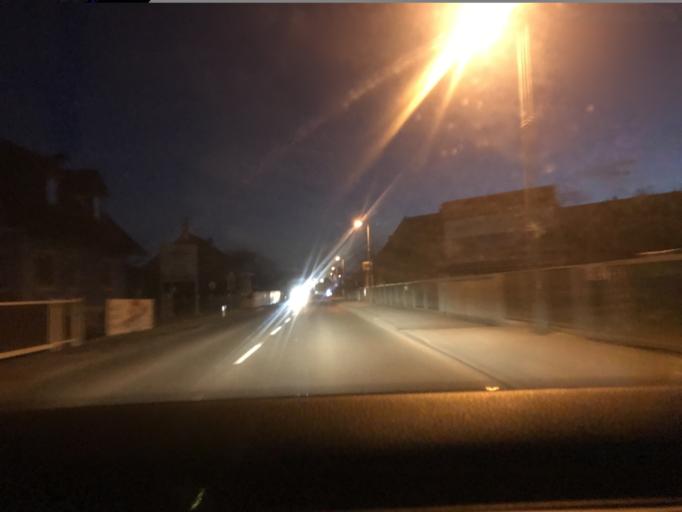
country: AT
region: Styria
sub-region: Politischer Bezirk Leibnitz
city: Kaindorf an der Sulm
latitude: 46.7890
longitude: 15.5485
